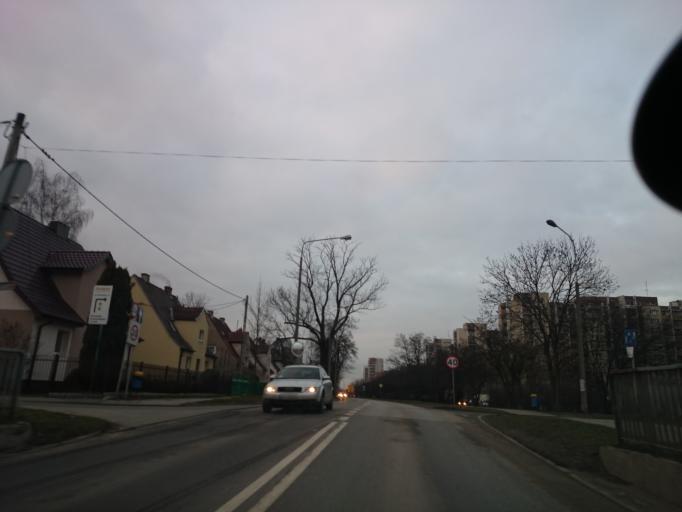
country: PL
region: Opole Voivodeship
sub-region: Powiat opolski
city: Opole
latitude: 50.6618
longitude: 17.9037
